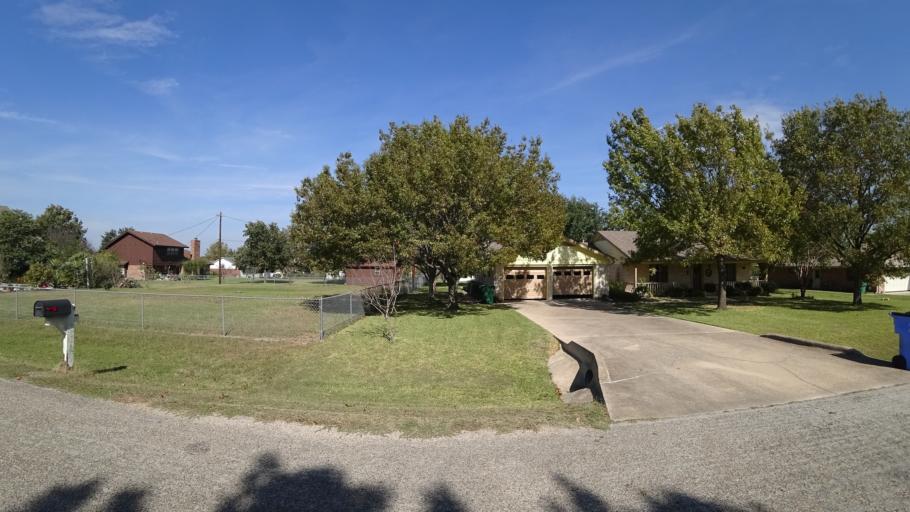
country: US
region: Texas
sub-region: Travis County
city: Pflugerville
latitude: 30.4197
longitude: -97.6255
